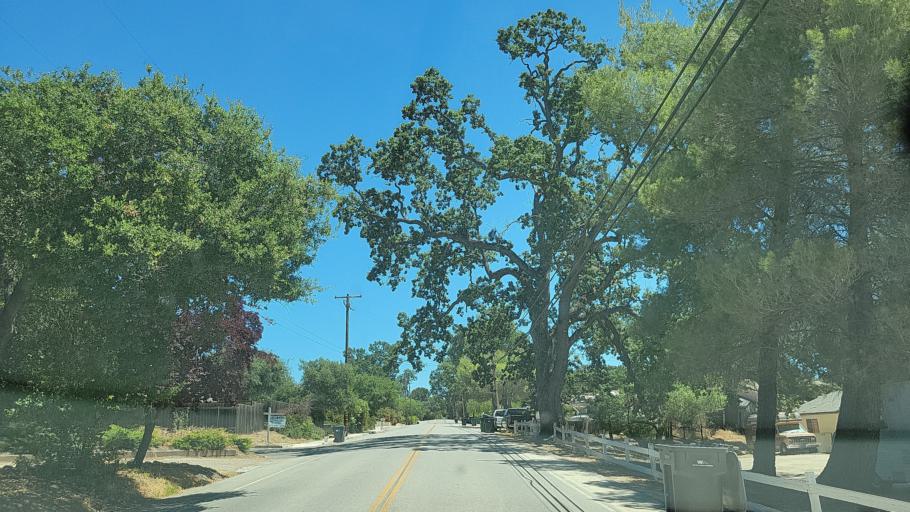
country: US
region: California
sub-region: San Luis Obispo County
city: Atascadero
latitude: 35.4704
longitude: -120.6620
